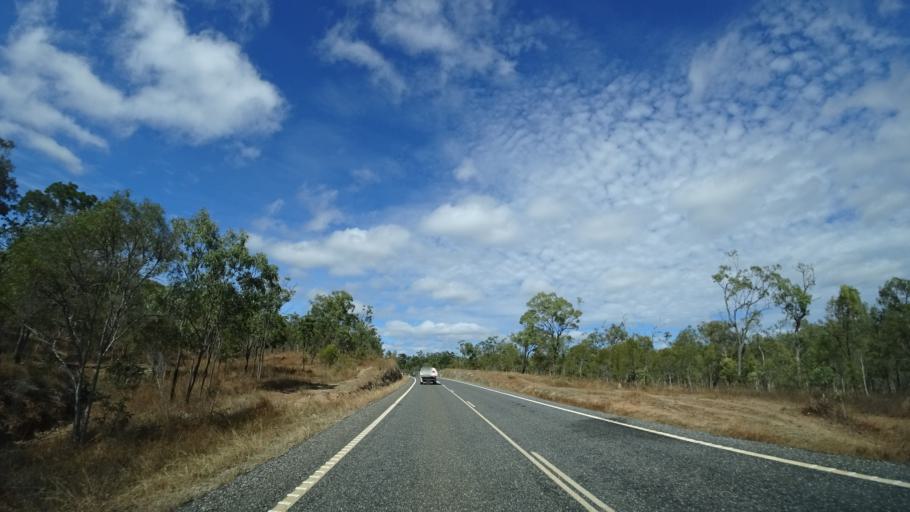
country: AU
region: Queensland
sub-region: Cairns
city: Port Douglas
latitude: -16.2995
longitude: 144.7153
